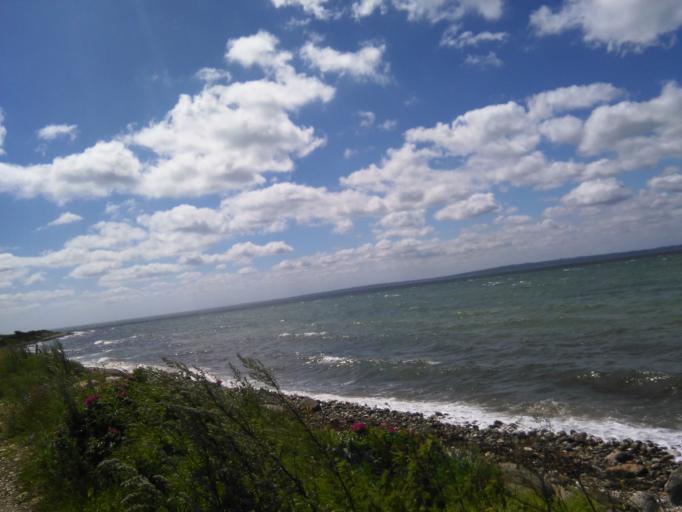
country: DK
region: Central Jutland
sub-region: Arhus Kommune
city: Logten
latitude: 56.1721
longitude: 10.3786
